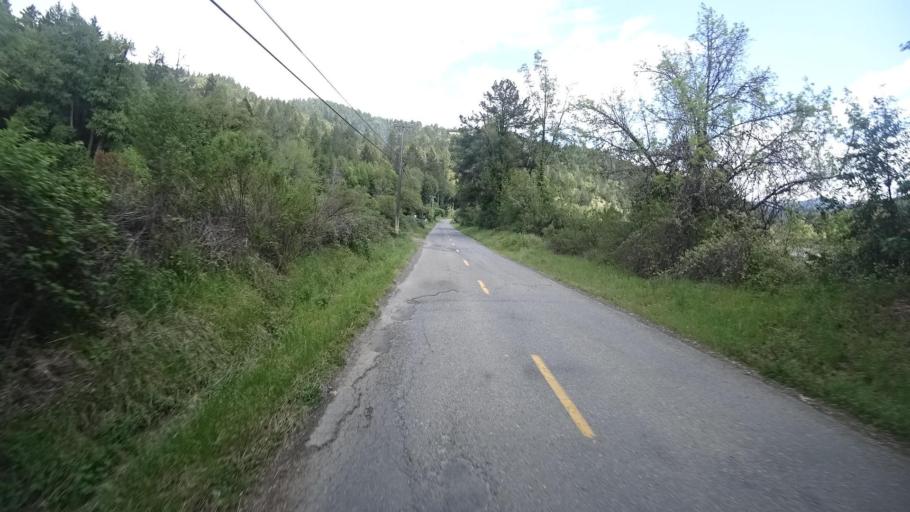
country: US
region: California
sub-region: Humboldt County
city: Redway
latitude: 40.0741
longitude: -123.8282
